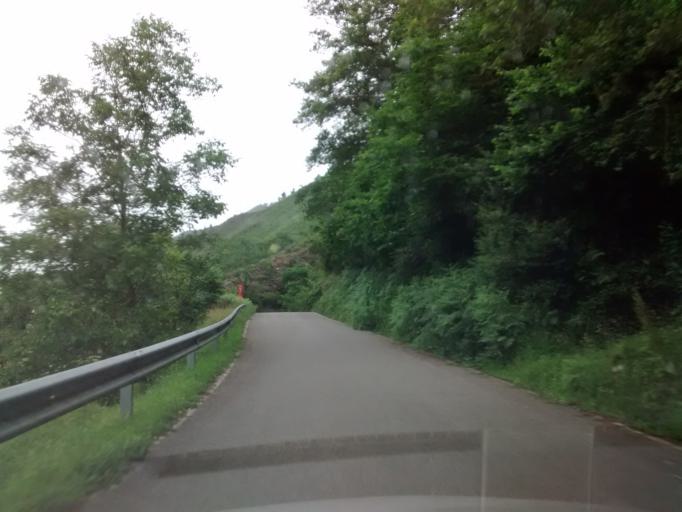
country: ES
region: Asturias
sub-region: Province of Asturias
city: Pilona
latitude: 43.2838
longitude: -5.3516
